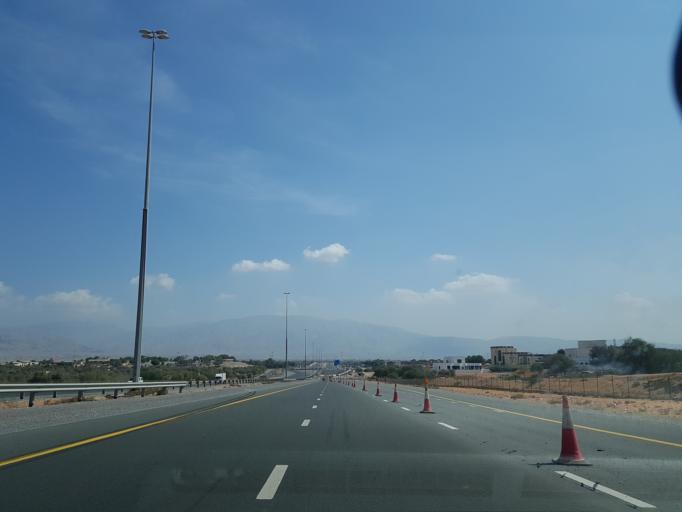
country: AE
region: Ra's al Khaymah
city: Ras al-Khaimah
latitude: 25.7034
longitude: 55.9556
